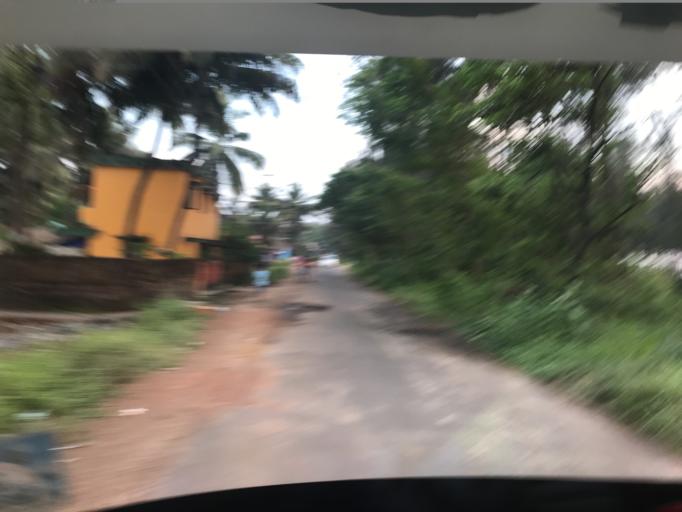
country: IN
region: Karnataka
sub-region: Dakshina Kannada
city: Mangalore
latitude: 12.8902
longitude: 74.8156
